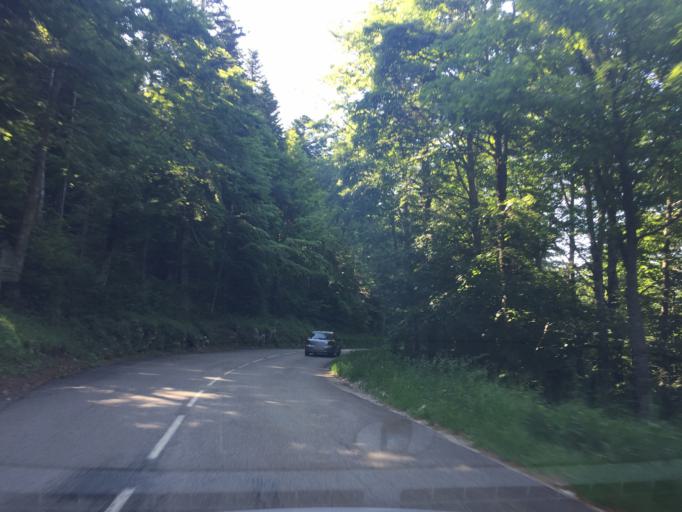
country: FR
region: Rhone-Alpes
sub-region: Departement de la Drome
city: Saint-Jean-en-Royans
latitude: 44.9284
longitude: 5.3200
